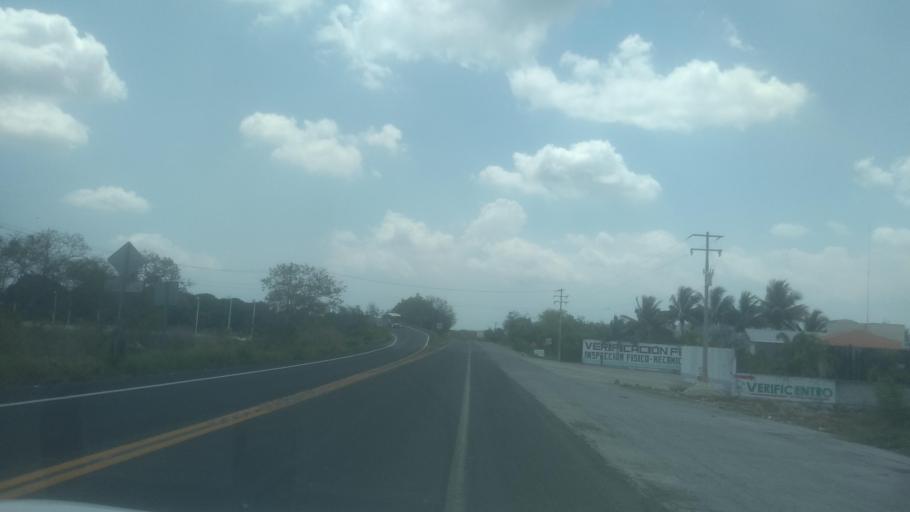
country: MX
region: Veracruz
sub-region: Emiliano Zapata
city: Plan del Rio
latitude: 19.3931
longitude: -96.6169
